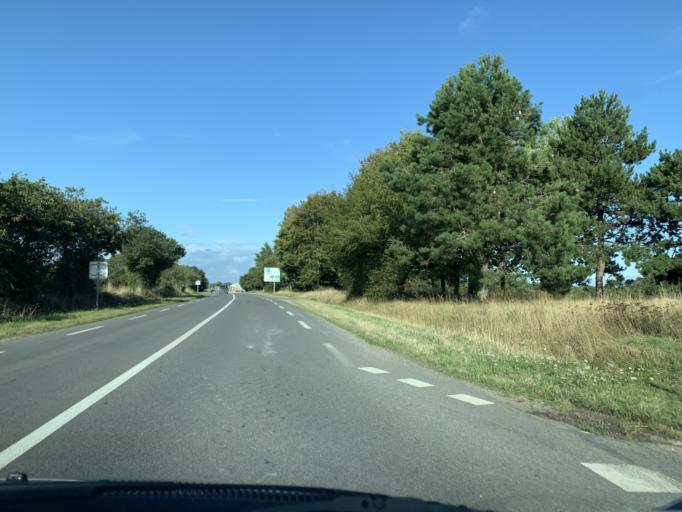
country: FR
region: Brittany
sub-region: Departement du Morbihan
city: Nivillac
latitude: 47.5043
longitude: -2.3051
